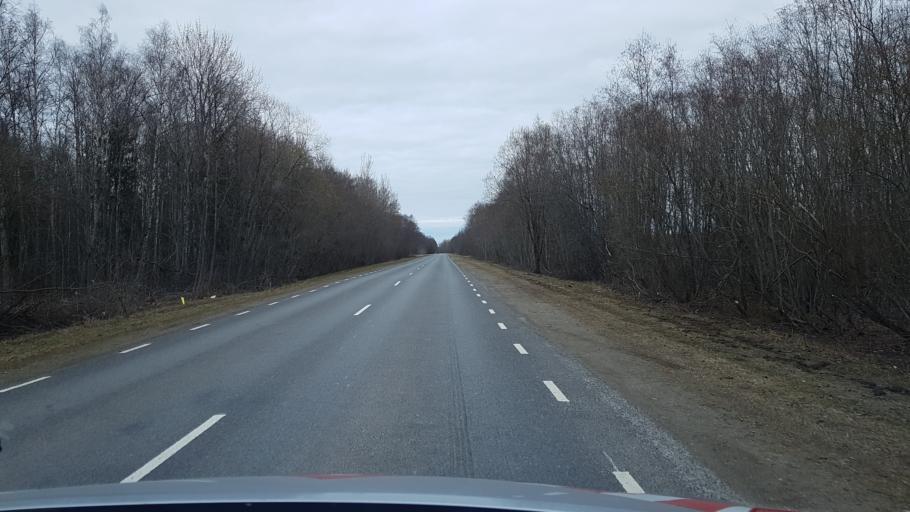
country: EE
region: Ida-Virumaa
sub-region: Sillamaee linn
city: Sillamae
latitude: 59.3554
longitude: 27.7480
